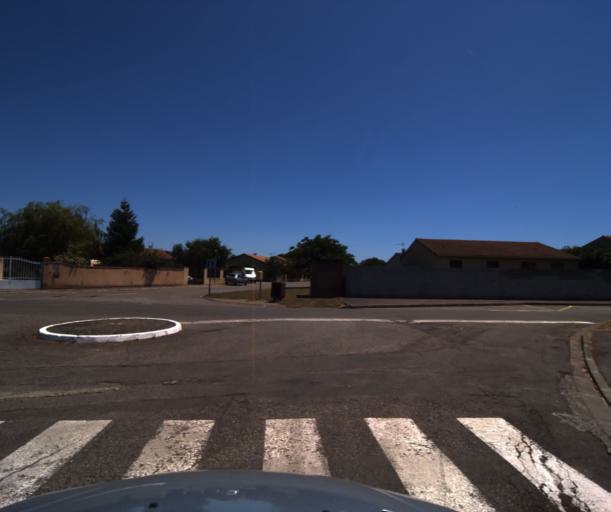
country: FR
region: Midi-Pyrenees
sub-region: Departement de la Haute-Garonne
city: Muret
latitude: 43.4566
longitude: 1.3415
